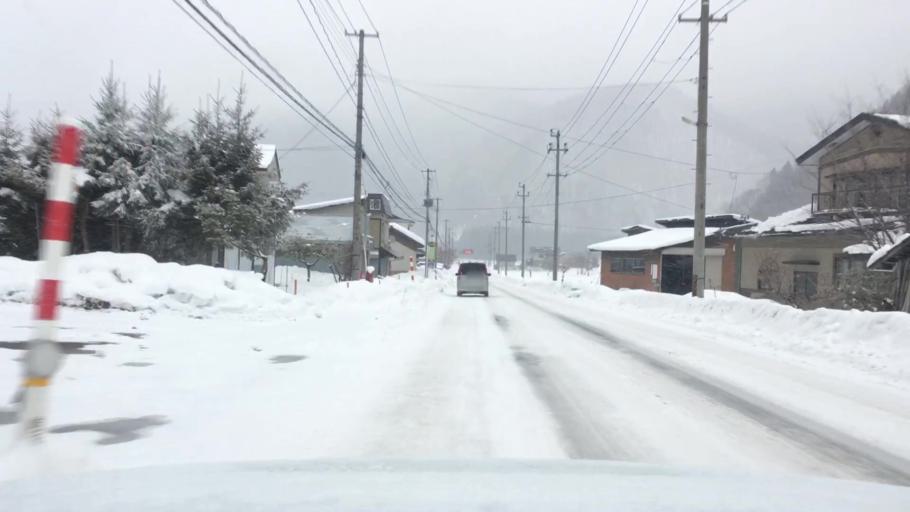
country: JP
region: Akita
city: Hanawa
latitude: 40.0760
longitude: 141.0211
